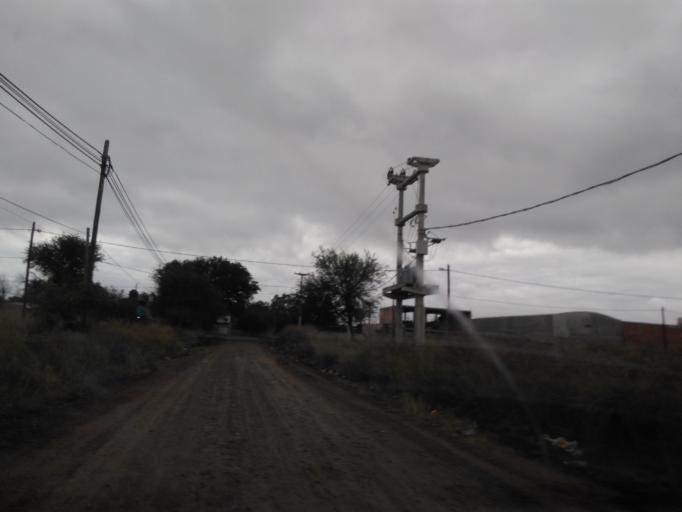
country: AR
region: Chaco
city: Fontana
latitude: -27.4504
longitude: -59.0321
